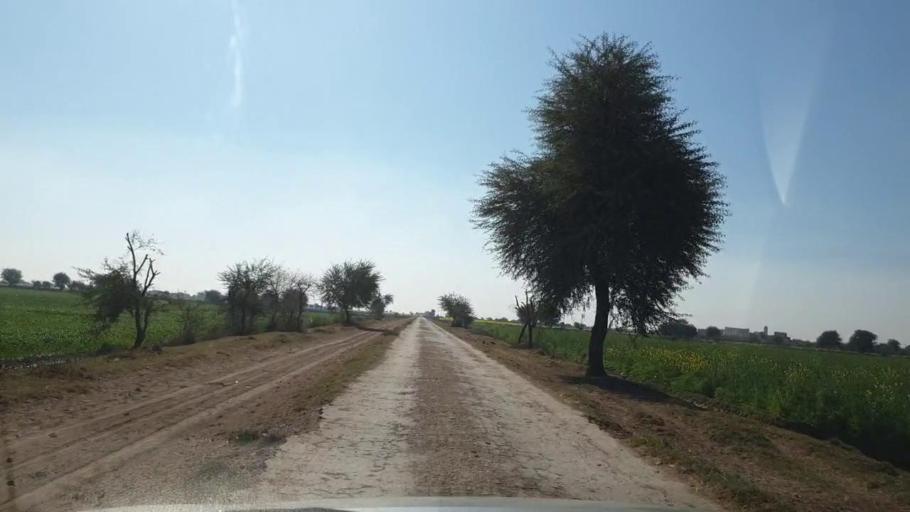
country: PK
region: Sindh
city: Jhol
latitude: 25.8131
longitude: 69.0357
